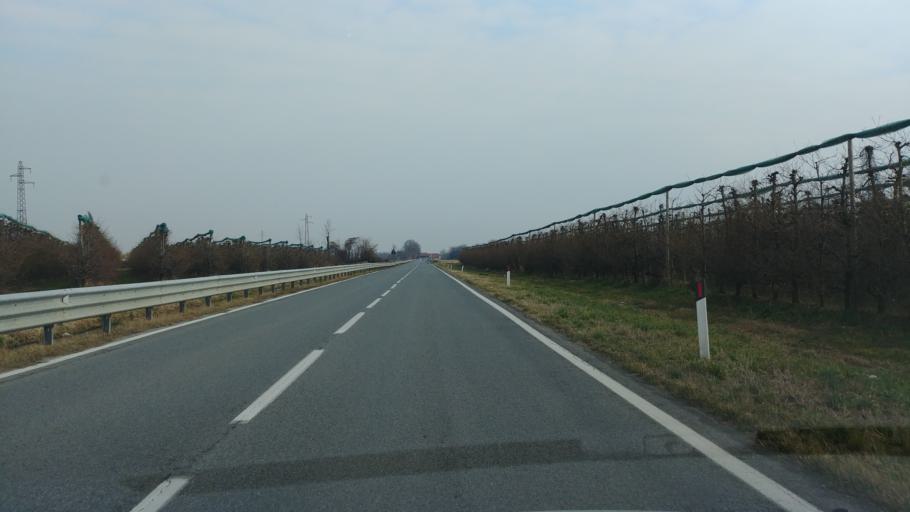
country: IT
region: Piedmont
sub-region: Provincia di Cuneo
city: Castelletto Stura
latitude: 44.4431
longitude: 7.6063
